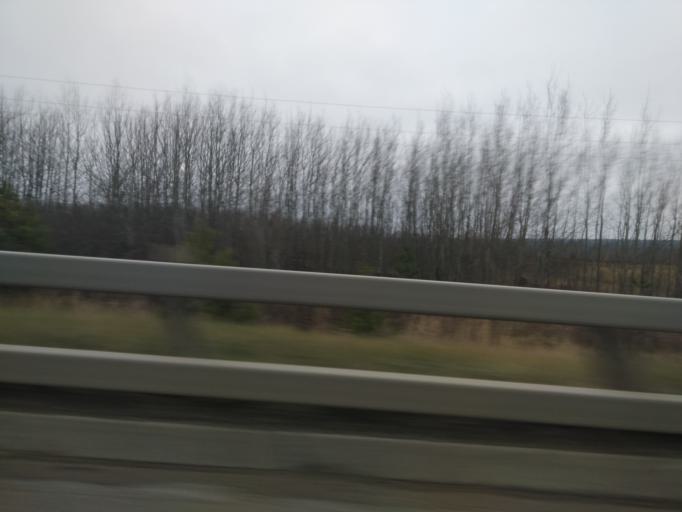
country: RU
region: Kirov
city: Krasnaya Polyana
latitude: 56.2297
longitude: 51.2121
